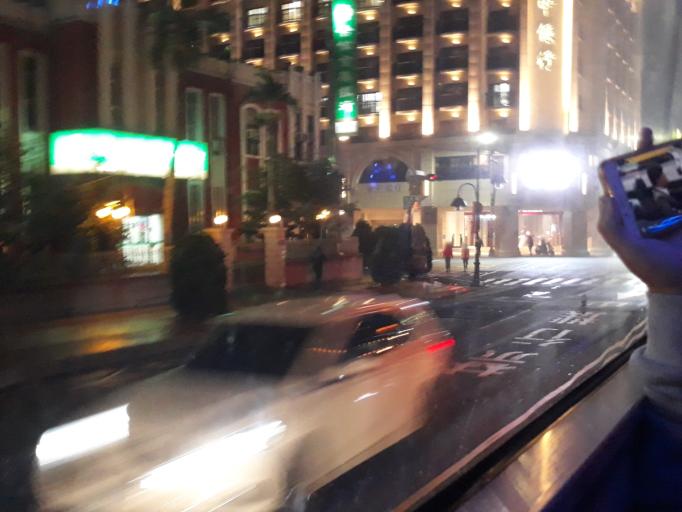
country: TW
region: Taiwan
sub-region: Taichung City
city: Taichung
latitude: 24.1382
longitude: 120.6803
